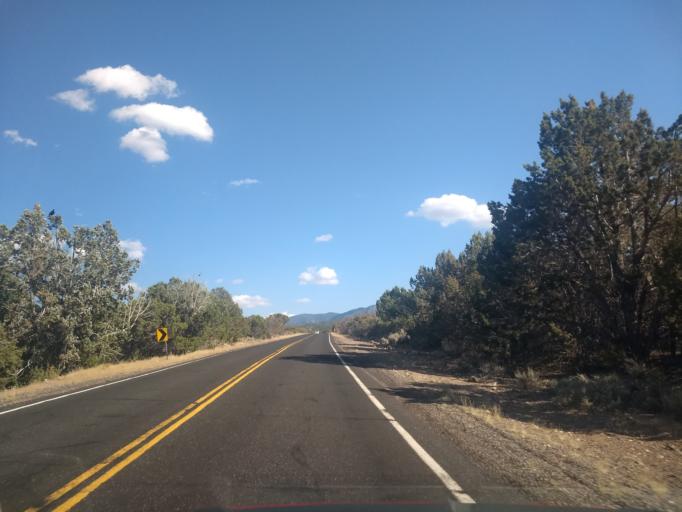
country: US
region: Utah
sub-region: Washington County
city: Enterprise
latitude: 37.4214
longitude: -113.5767
